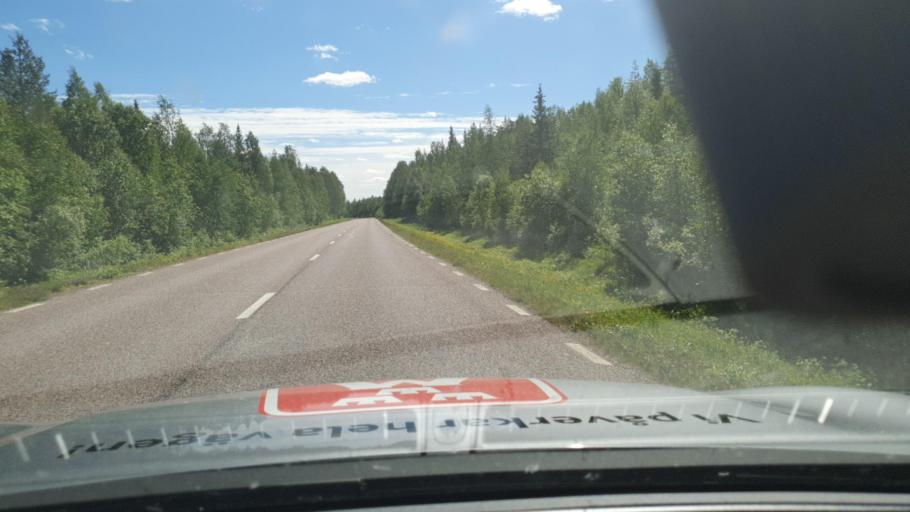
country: FI
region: Lapland
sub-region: Tunturi-Lappi
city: Kolari
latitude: 67.0533
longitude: 23.6782
